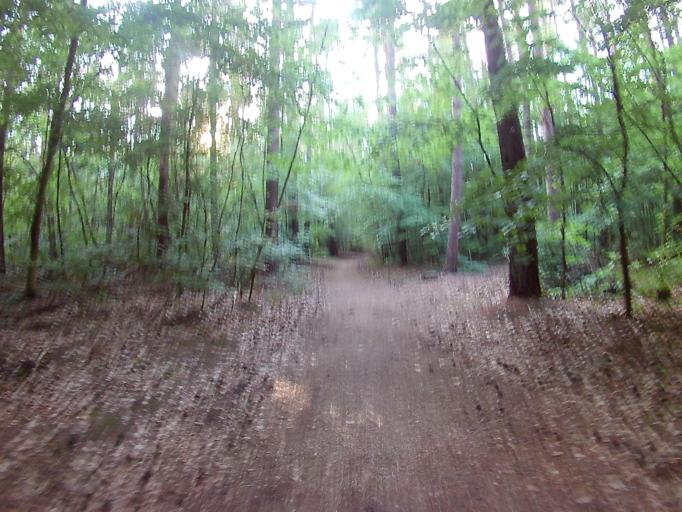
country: DE
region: Mecklenburg-Vorpommern
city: Koserow
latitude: 54.0422
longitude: 14.0198
